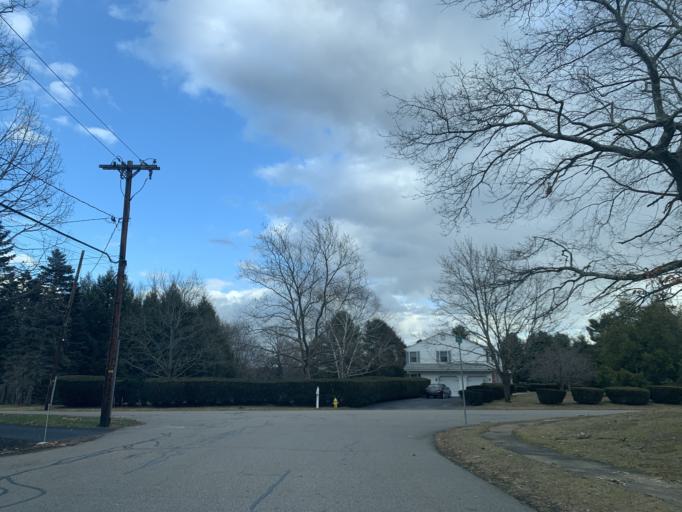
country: US
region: Massachusetts
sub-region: Norfolk County
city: Dedham
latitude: 42.2126
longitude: -71.1636
